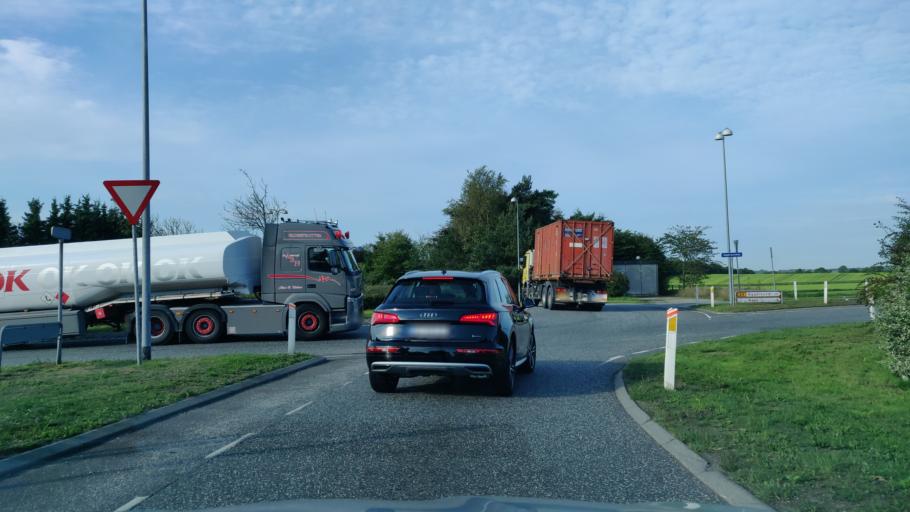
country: DK
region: North Denmark
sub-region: Vesthimmerland Kommune
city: Aars
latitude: 56.7729
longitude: 9.5698
